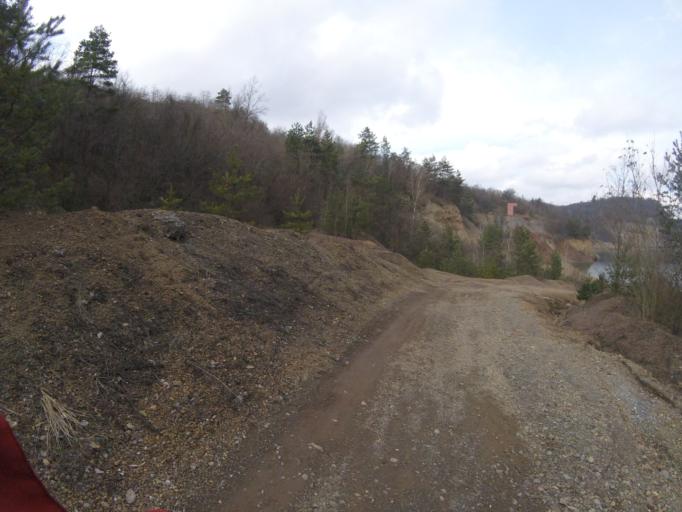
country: HU
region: Borsod-Abauj-Zemplen
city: Rudabanya
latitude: 48.3904
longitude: 20.6343
